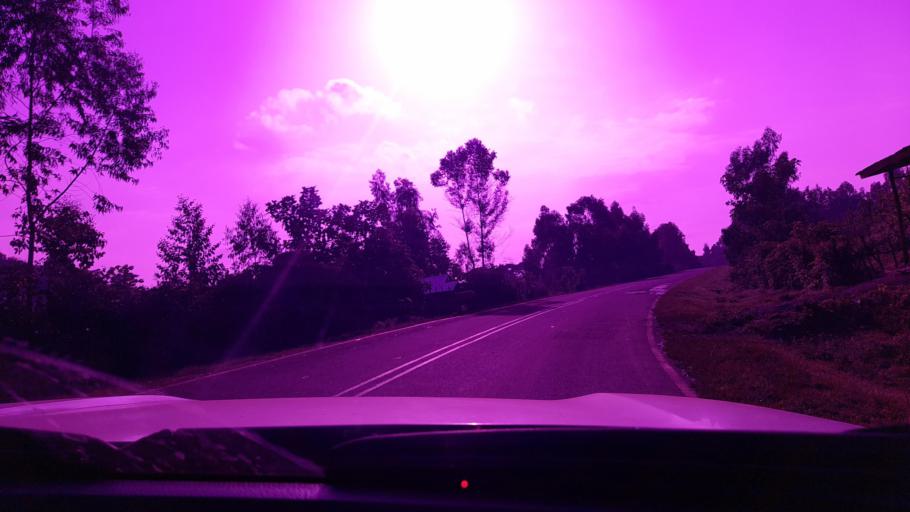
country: ET
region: Oromiya
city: Bedele
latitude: 8.1508
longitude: 36.4608
